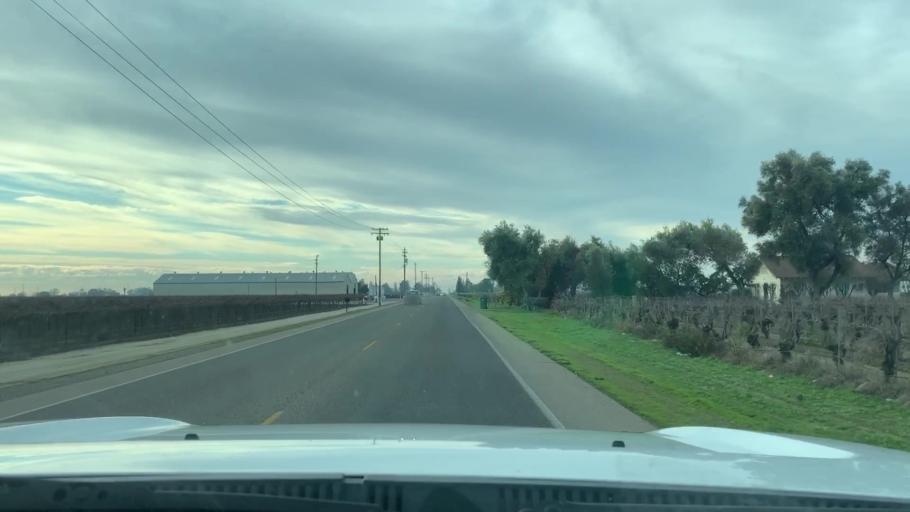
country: US
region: California
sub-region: Fresno County
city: Fowler
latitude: 36.6055
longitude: -119.7392
